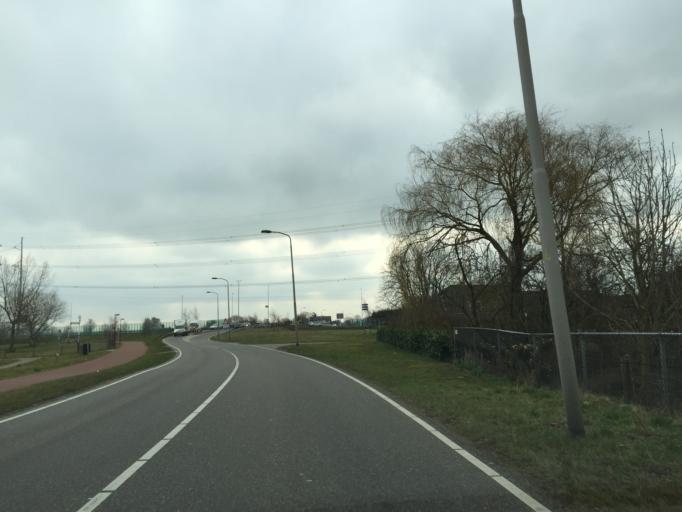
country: NL
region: South Holland
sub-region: Gemeente Zoetermeer
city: Zoetermeer
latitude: 52.0335
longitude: 4.4756
